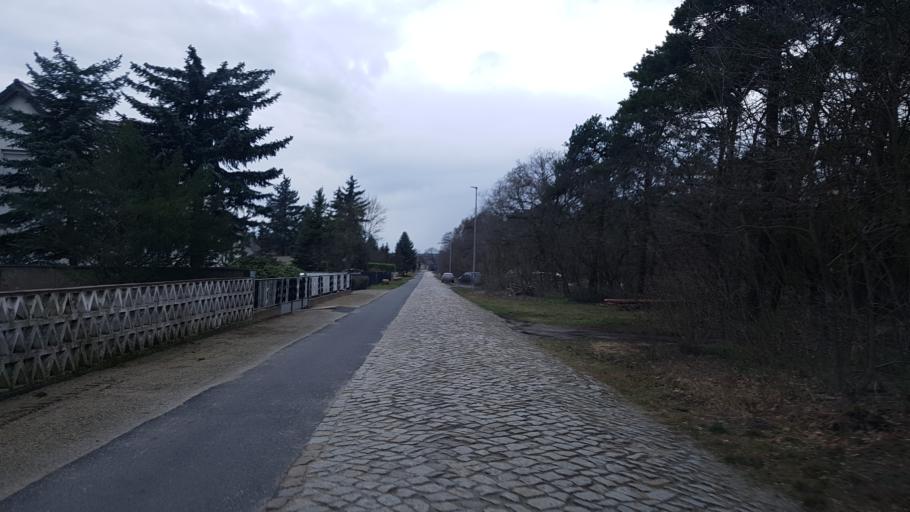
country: DE
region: Brandenburg
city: Hohenleipisch
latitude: 51.4741
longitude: 13.5782
